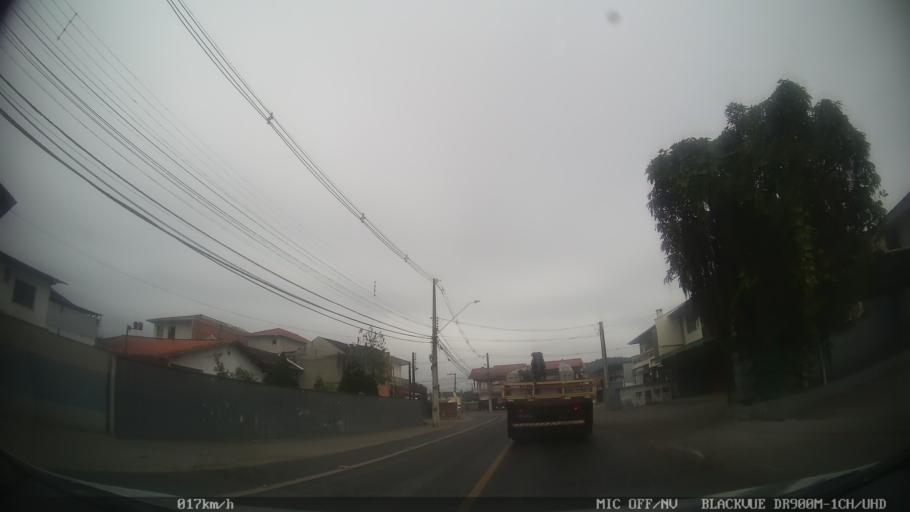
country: BR
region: Santa Catarina
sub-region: Joinville
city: Joinville
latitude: -26.2469
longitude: -48.8103
